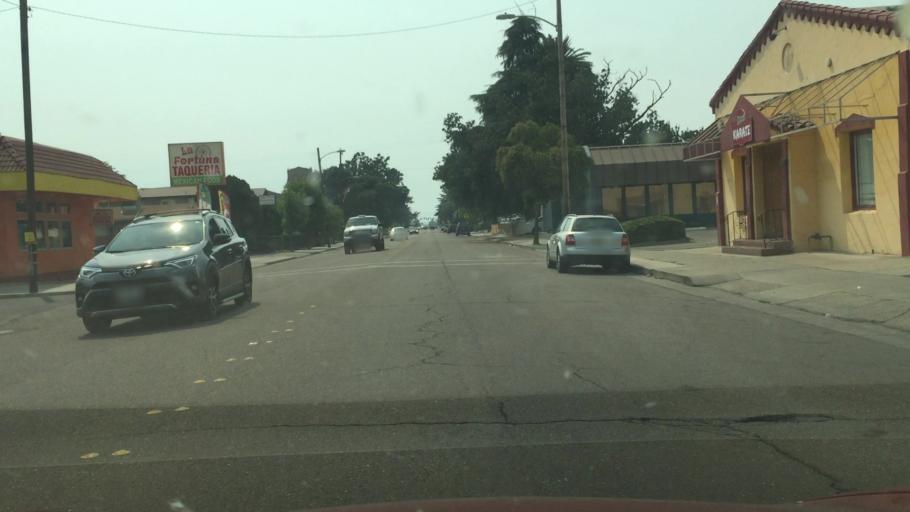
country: US
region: California
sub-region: San Joaquin County
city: Manteca
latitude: 37.7975
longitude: -121.2217
